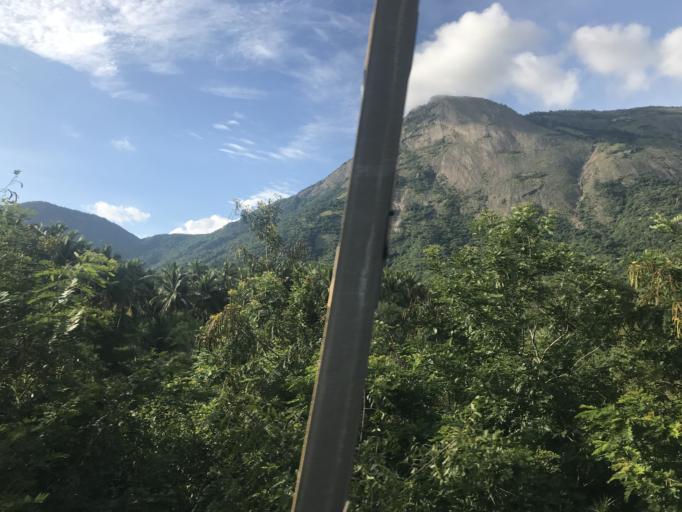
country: IN
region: Tamil Nadu
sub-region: Coimbatore
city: Madukkarai
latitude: 10.8953
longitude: 76.8855
